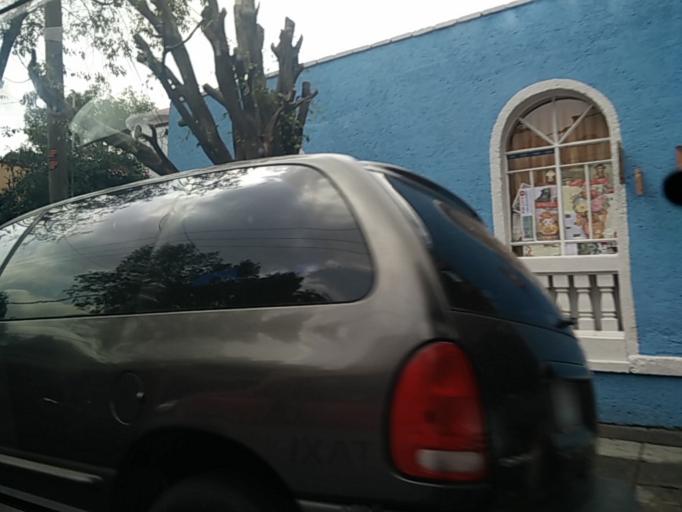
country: MX
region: Mexico City
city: Coyoacan
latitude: 19.3477
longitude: -99.1642
